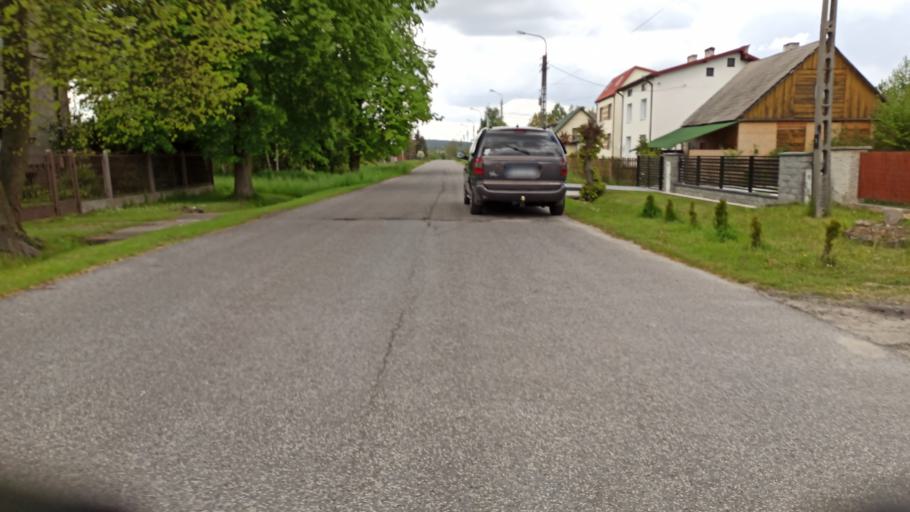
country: PL
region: Swietokrzyskie
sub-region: Powiat skarzyski
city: Skarzysko Koscielne
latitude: 51.1380
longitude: 20.9093
